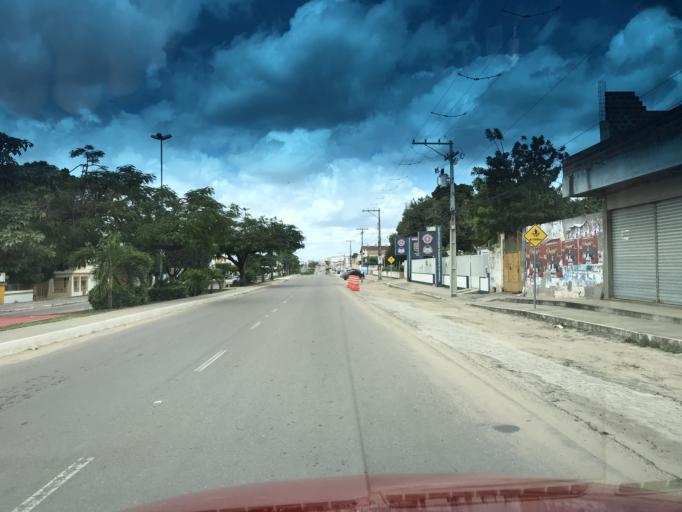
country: BR
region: Bahia
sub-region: Itaberaba
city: Itaberaba
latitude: -12.5199
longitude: -40.3059
